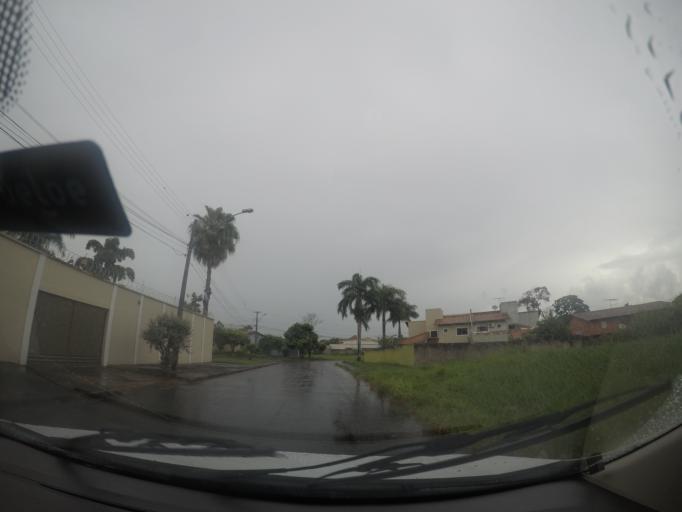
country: BR
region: Goias
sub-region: Goiania
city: Goiania
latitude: -16.6453
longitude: -49.2303
